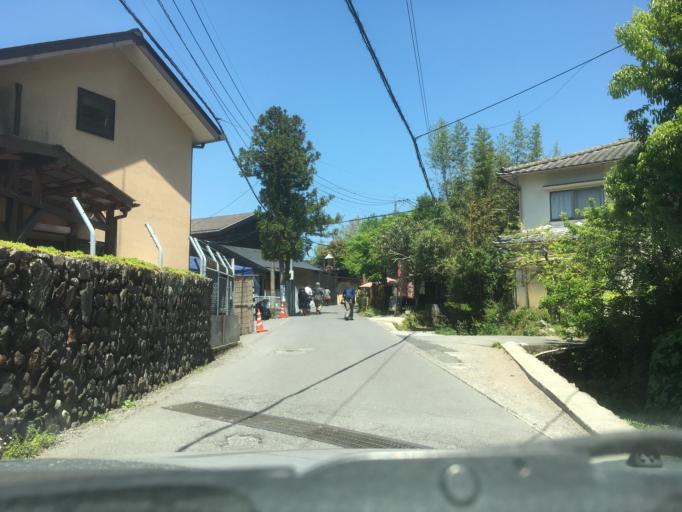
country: JP
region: Oita
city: Beppu
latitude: 33.2676
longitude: 131.3679
